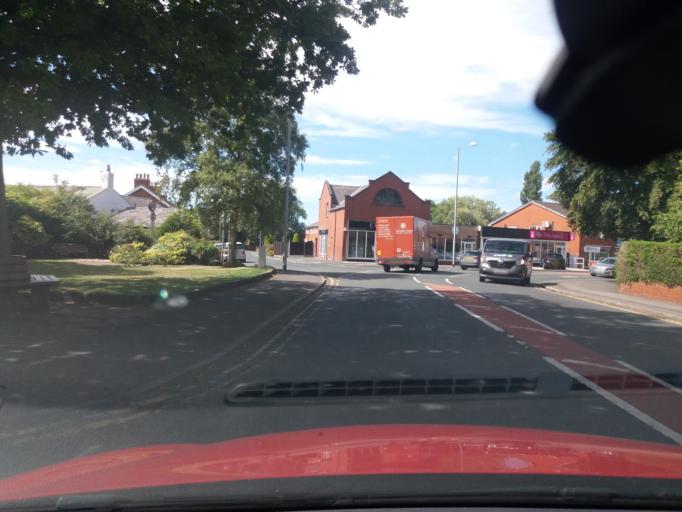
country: GB
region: England
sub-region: Lancashire
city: Euxton
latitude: 53.6435
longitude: -2.7234
